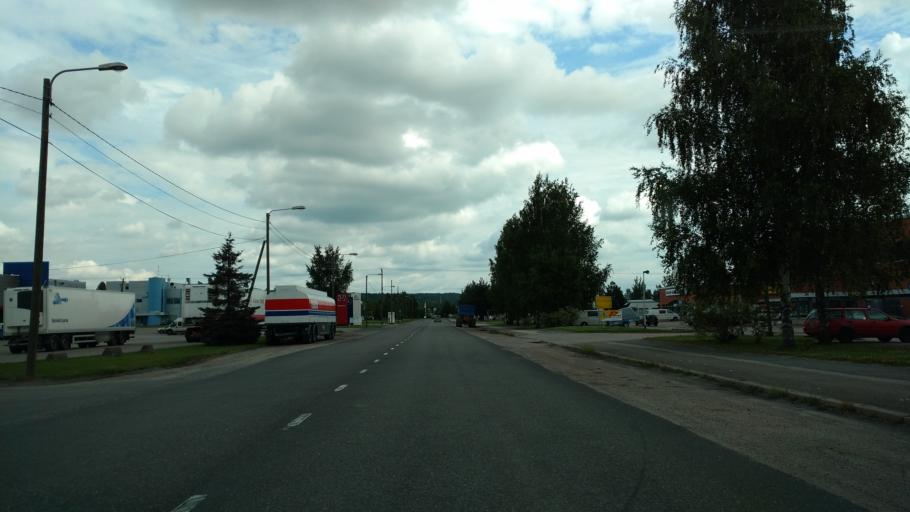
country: FI
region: Varsinais-Suomi
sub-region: Salo
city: Halikko
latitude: 60.3845
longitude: 23.1011
